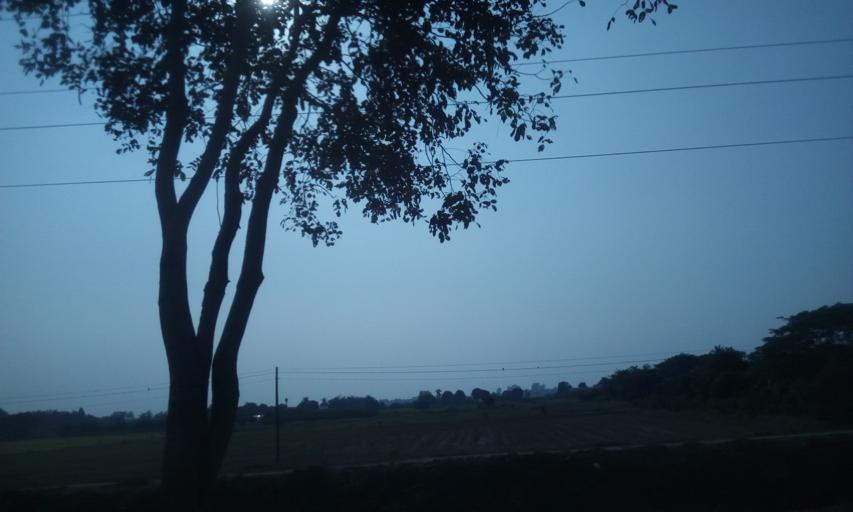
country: TH
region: Sing Buri
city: Tha Chang
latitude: 14.7228
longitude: 100.4305
